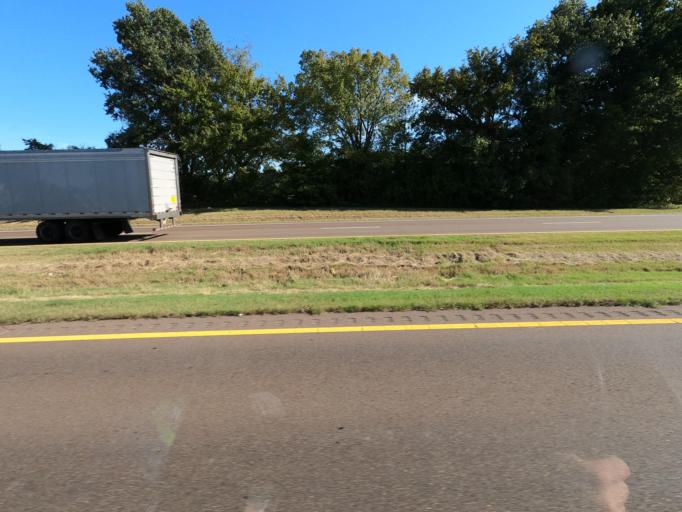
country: US
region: Tennessee
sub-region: Obion County
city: Englewood
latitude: 36.3890
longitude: -89.1033
